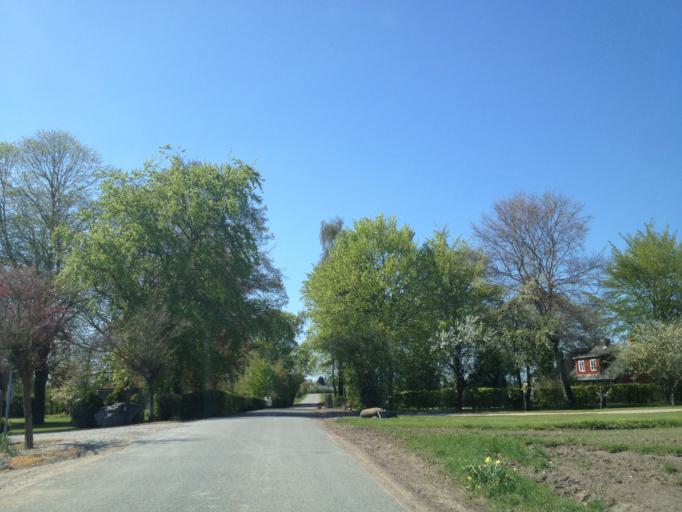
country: DK
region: Zealand
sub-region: Roskilde Kommune
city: Viby
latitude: 55.5338
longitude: 12.0372
